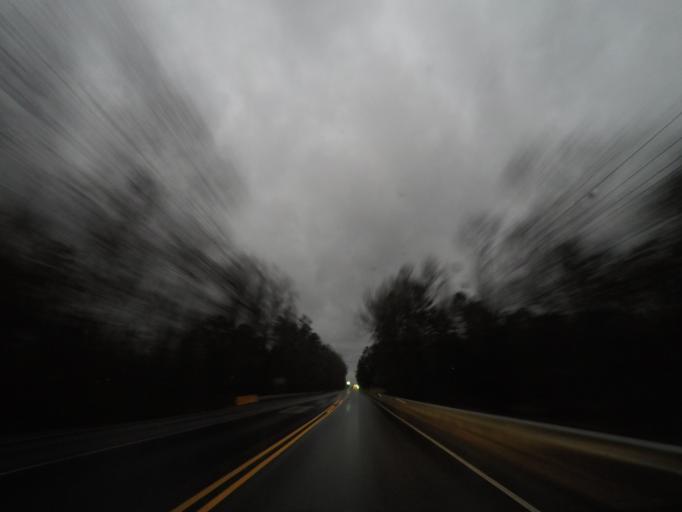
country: US
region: North Carolina
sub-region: Orange County
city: Hillsborough
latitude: 36.0854
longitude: -79.0936
